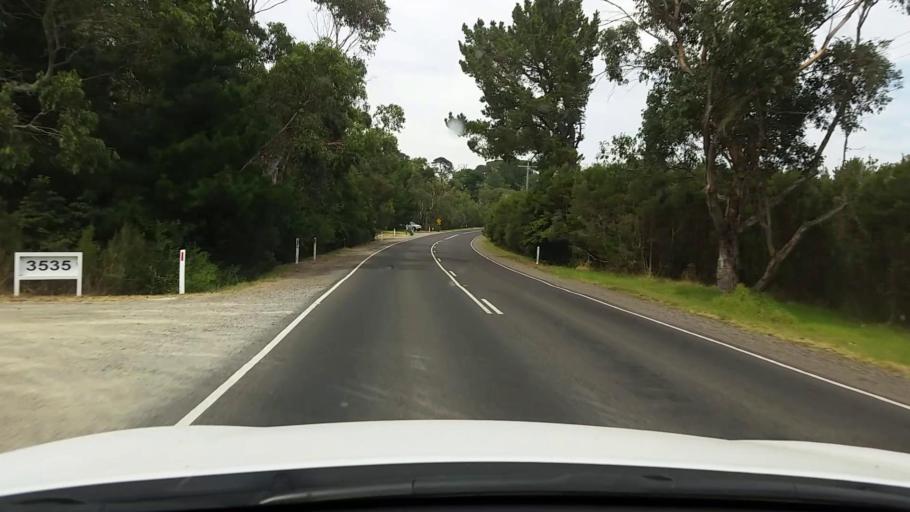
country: AU
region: Victoria
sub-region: Mornington Peninsula
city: Merricks
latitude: -38.3967
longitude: 145.0837
